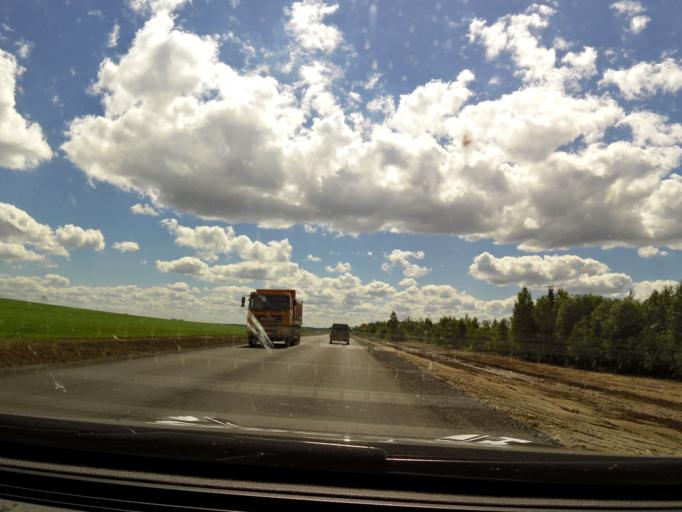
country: RU
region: Vologda
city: Molochnoye
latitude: 59.2972
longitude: 39.6880
